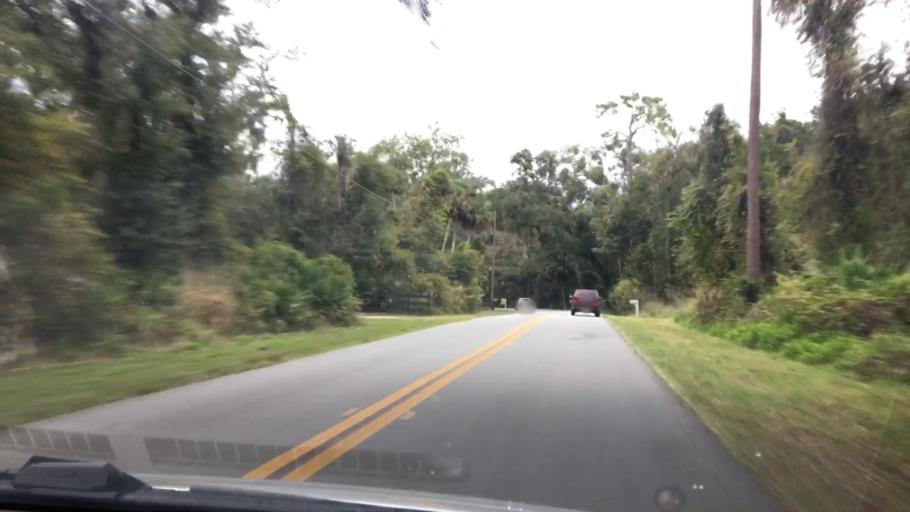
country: US
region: Florida
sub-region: Seminole County
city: Midway
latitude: 28.8558
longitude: -81.2100
